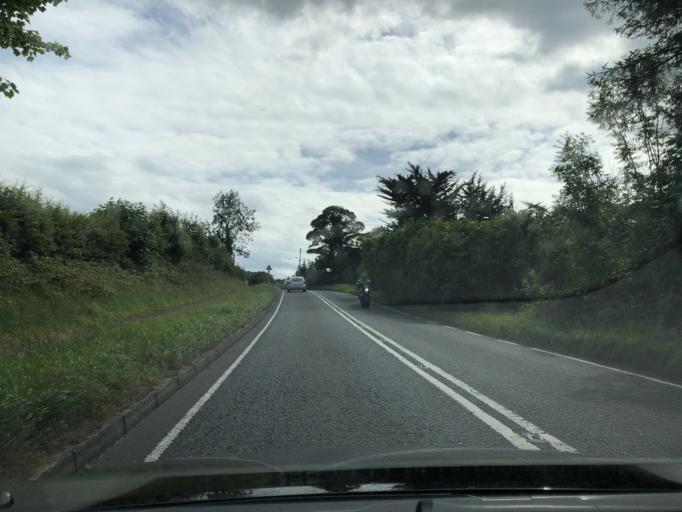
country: GB
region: Northern Ireland
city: Ballynahinch
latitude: 54.3672
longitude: -5.8603
